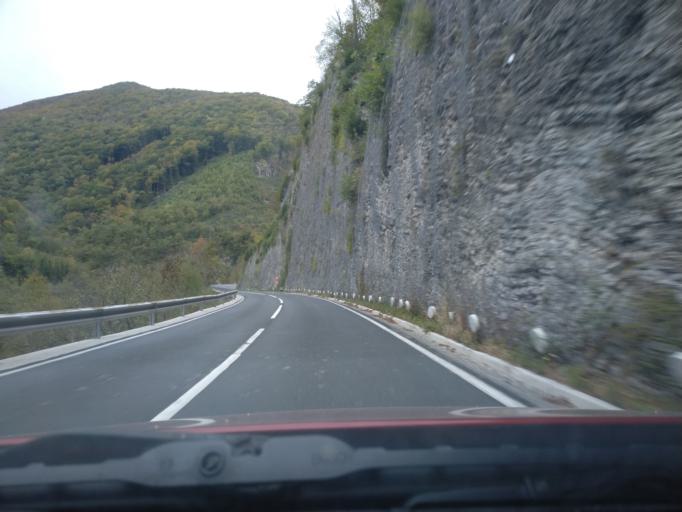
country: SI
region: Tolmin
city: Tolmin
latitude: 46.1286
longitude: 13.7130
